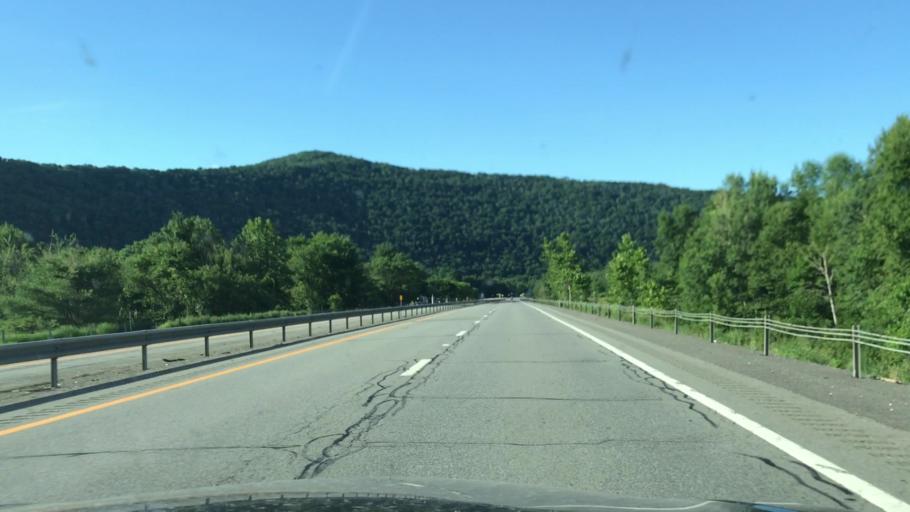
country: US
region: New York
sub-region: Delaware County
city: Hancock
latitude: 41.9889
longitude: -75.1618
